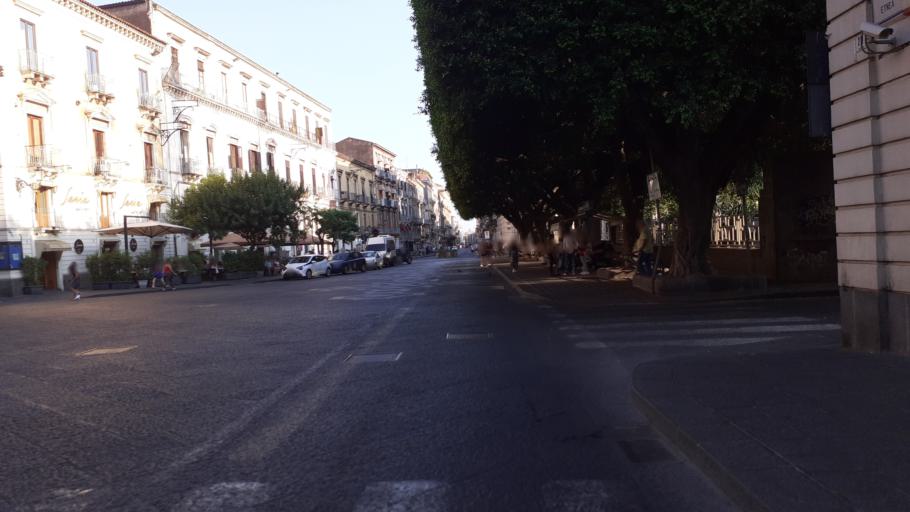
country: IT
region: Sicily
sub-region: Catania
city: Catania
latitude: 37.5112
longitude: 15.0853
